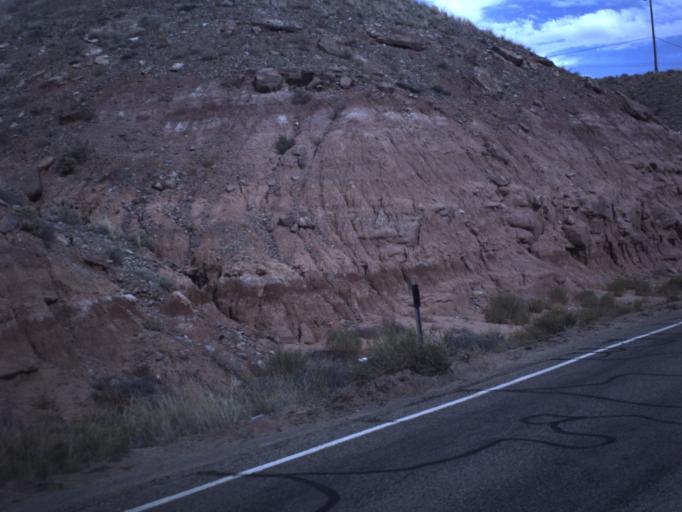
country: US
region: Colorado
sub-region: Montezuma County
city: Towaoc
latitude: 37.2252
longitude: -109.2078
